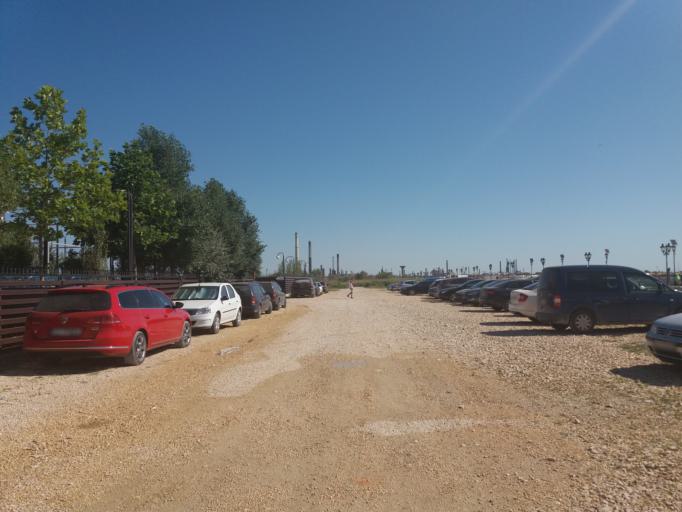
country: RO
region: Constanta
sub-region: Comuna Navodari
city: Navodari
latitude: 44.3205
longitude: 28.6353
